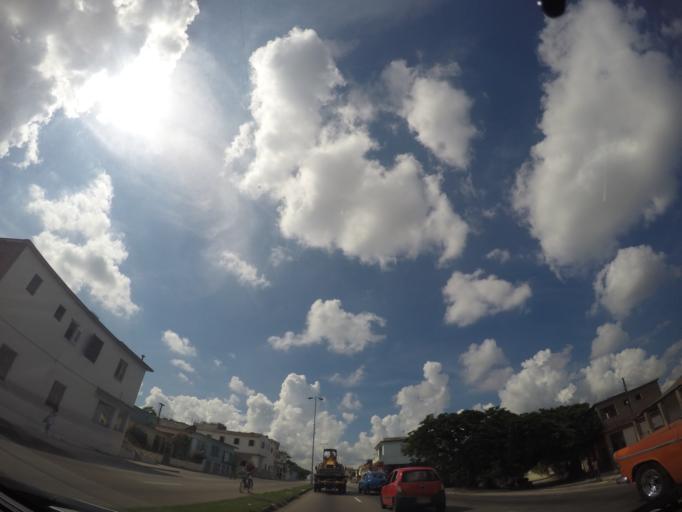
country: CU
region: La Habana
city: Cerro
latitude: 23.1004
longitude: -82.4207
